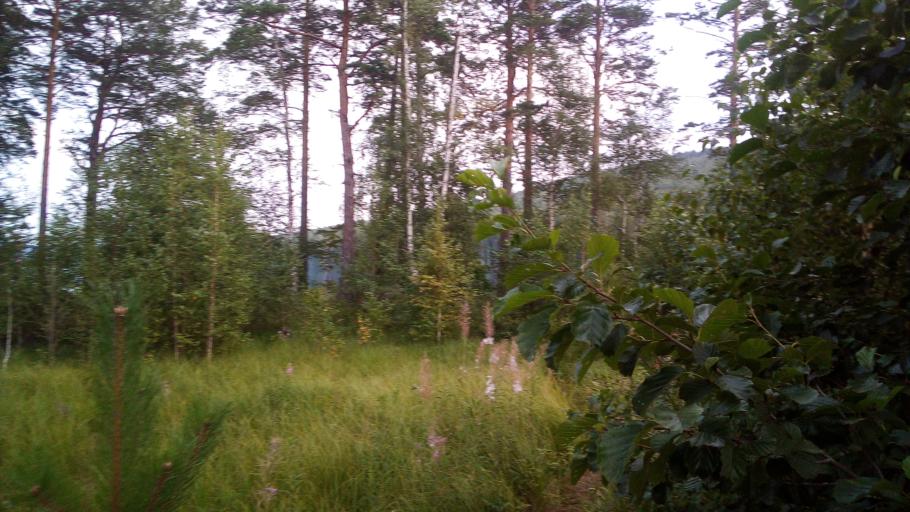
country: RU
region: Chelyabinsk
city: Turgoyak
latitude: 55.1607
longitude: 60.0294
